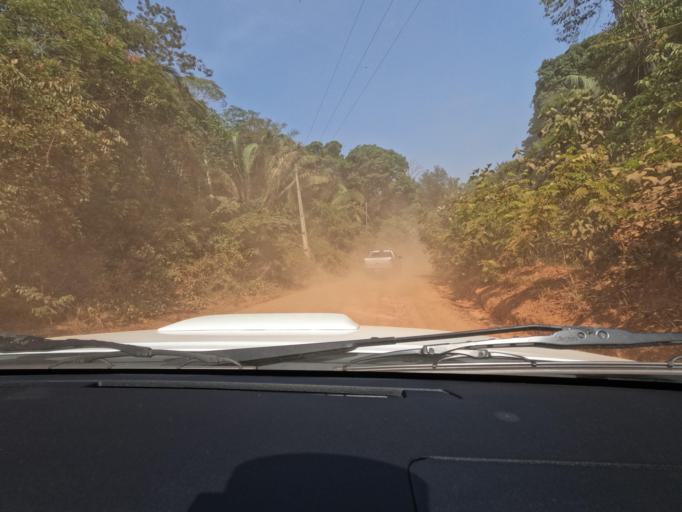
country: BR
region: Rondonia
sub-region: Porto Velho
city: Porto Velho
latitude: -8.6729
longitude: -64.0017
